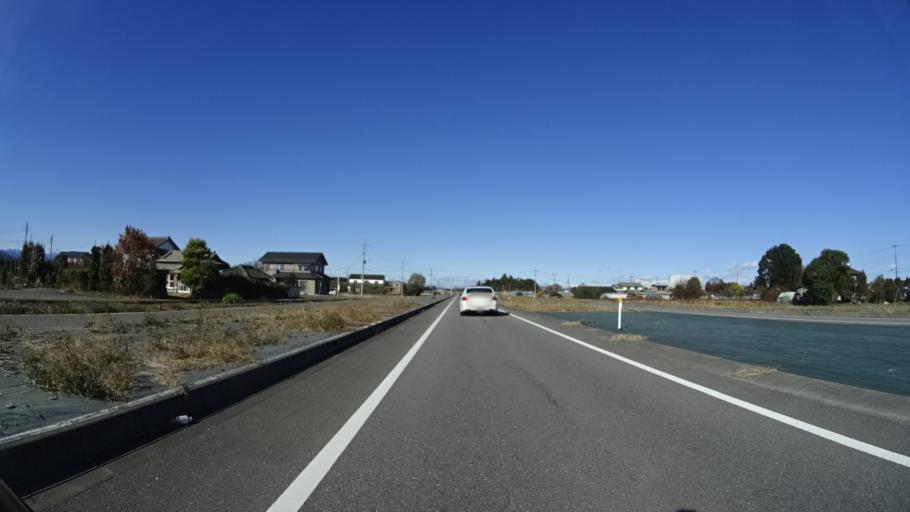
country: JP
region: Tochigi
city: Kanuma
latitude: 36.4821
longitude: 139.7537
